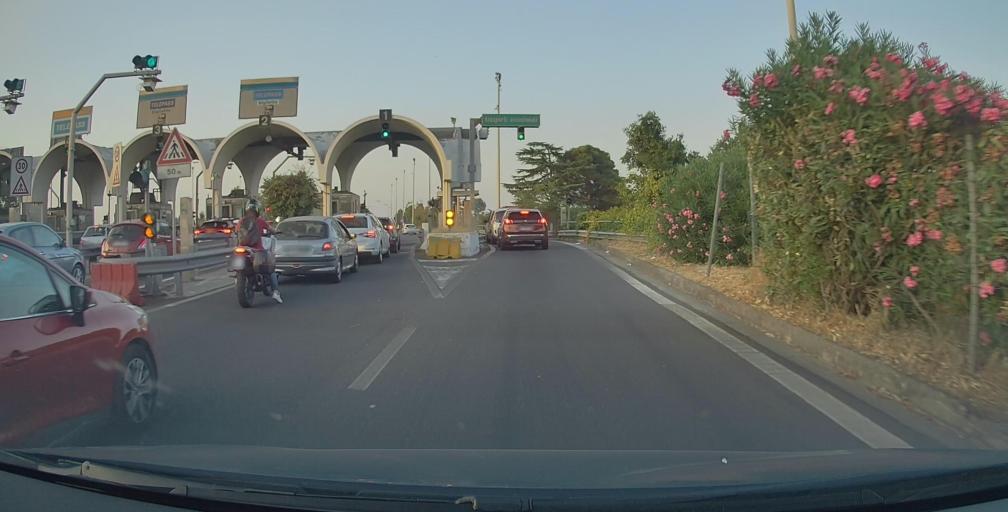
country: IT
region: Sicily
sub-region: Catania
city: San Gregorio di Catania
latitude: 37.5668
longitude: 15.1032
